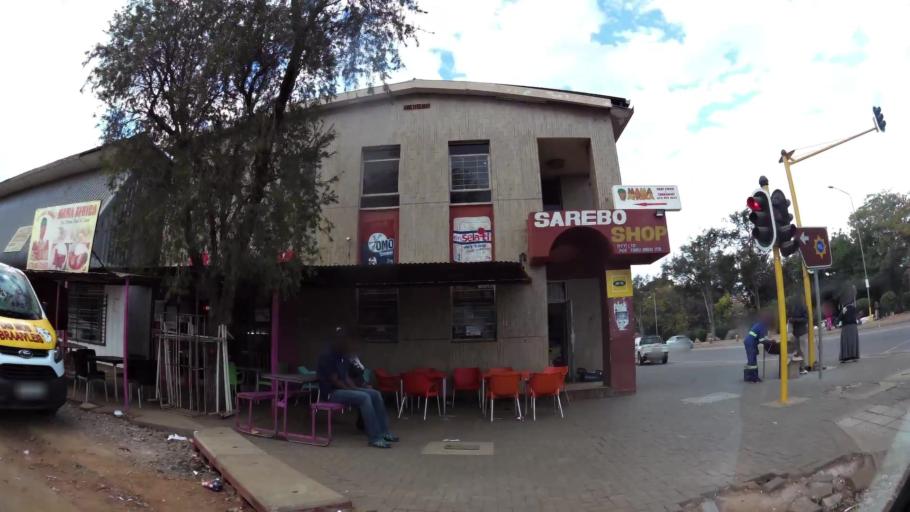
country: ZA
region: Limpopo
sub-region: Waterberg District Municipality
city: Modimolle
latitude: -24.5202
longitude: 28.7133
